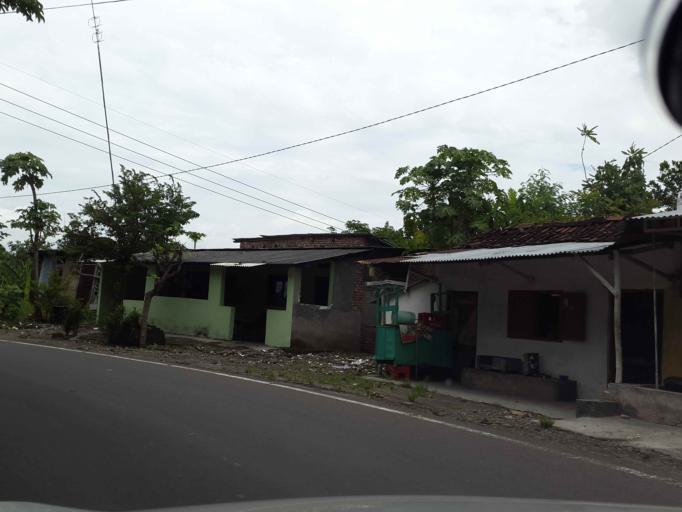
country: ID
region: East Java
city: Mojokerto
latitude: -7.4608
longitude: 112.4291
